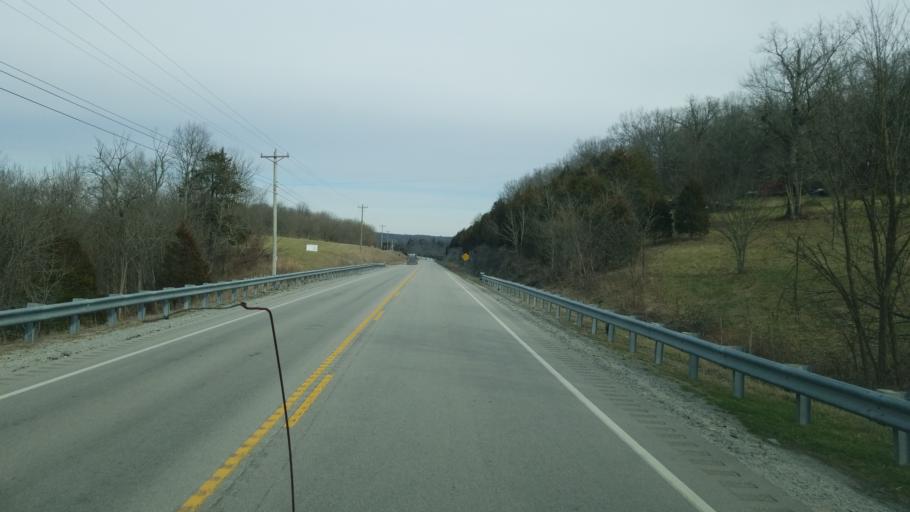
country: US
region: Kentucky
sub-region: Nicholas County
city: Carlisle
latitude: 38.4161
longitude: -84.0028
